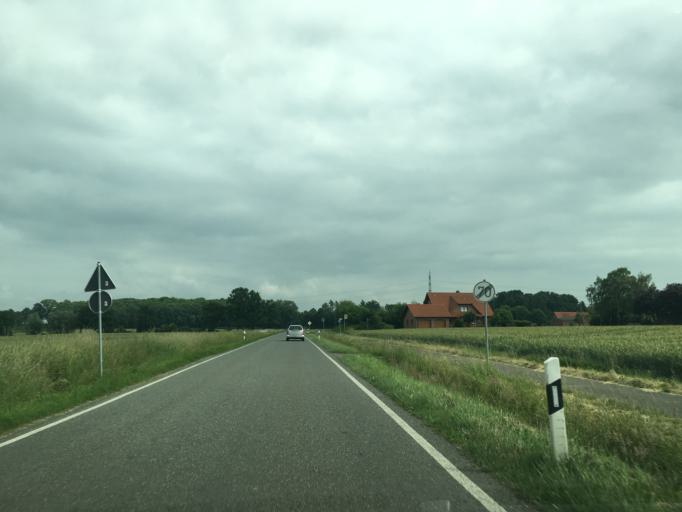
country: DE
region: North Rhine-Westphalia
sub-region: Regierungsbezirk Munster
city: Horstmar
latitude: 52.1056
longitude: 7.3127
